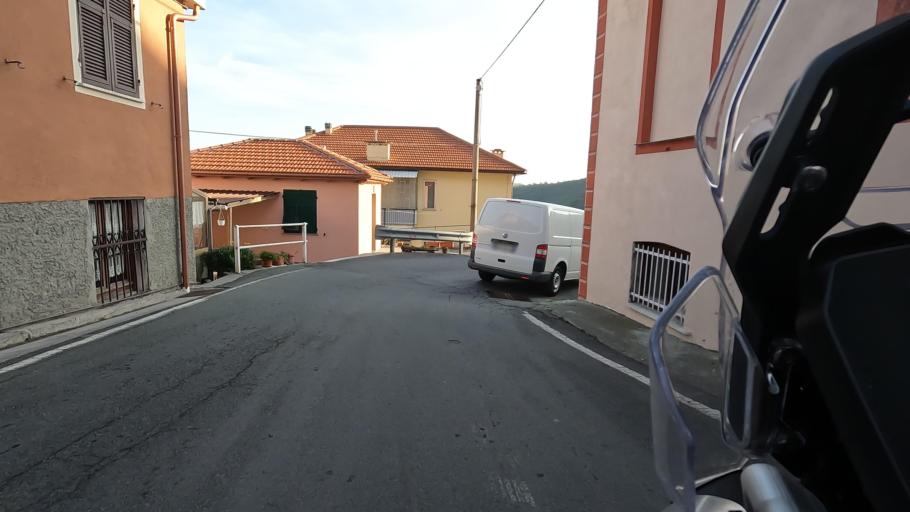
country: IT
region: Liguria
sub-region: Provincia di Savona
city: San Giovanni
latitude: 44.4033
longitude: 8.5343
